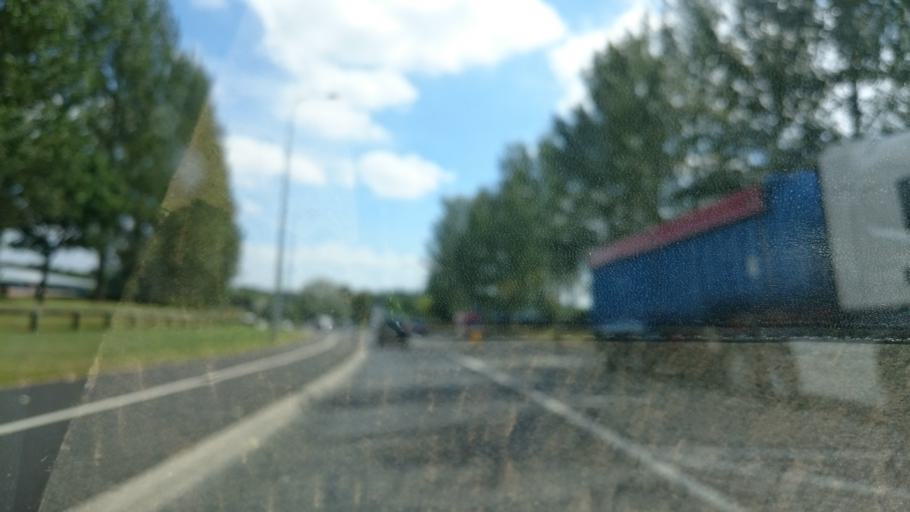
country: IE
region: Leinster
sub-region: Kilkenny
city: Kilkenny
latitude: 52.6483
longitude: -7.2230
